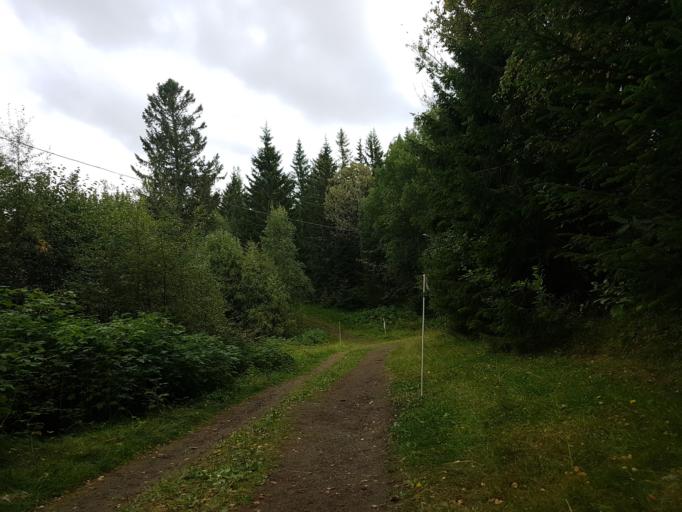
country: NO
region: Sor-Trondelag
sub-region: Skaun
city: Borsa
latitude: 63.4310
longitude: 10.1887
